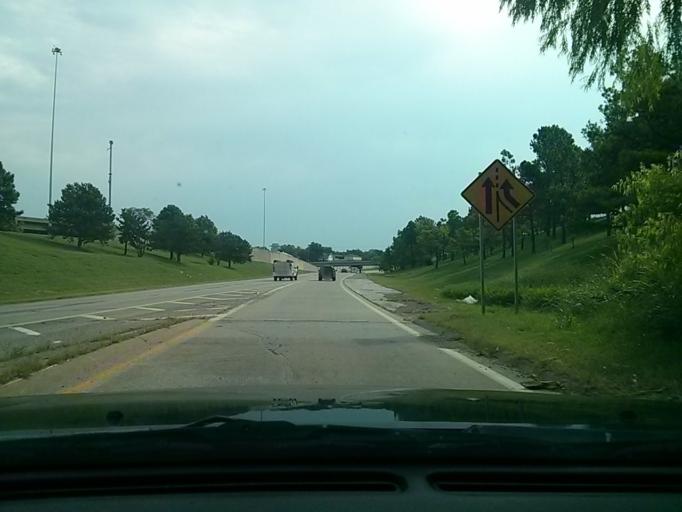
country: US
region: Oklahoma
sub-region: Tulsa County
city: Tulsa
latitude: 36.1416
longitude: -95.9799
